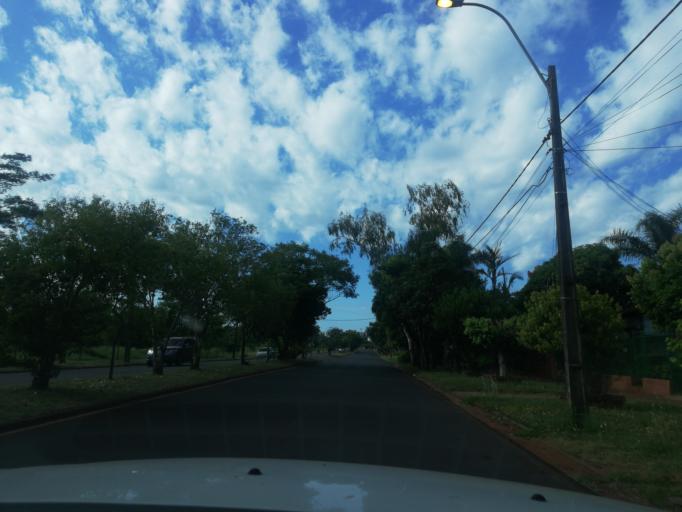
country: PY
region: Itapua
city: Encarnacion
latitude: -27.3502
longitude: -55.8490
